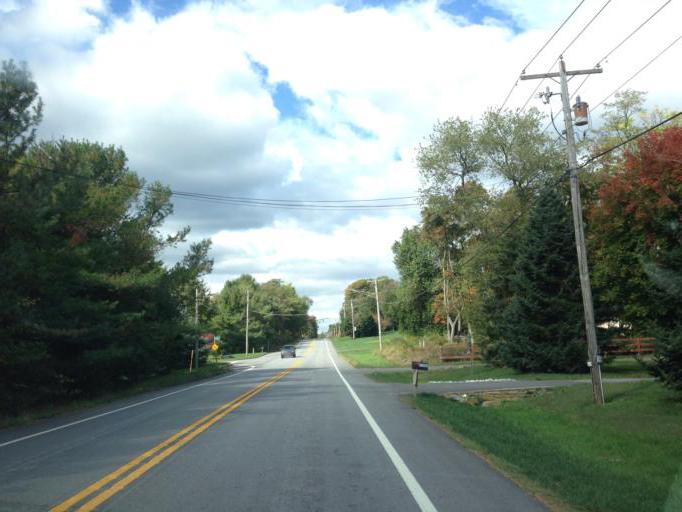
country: US
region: Maryland
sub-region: Carroll County
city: Mount Airy
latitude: 39.3492
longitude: -77.1158
